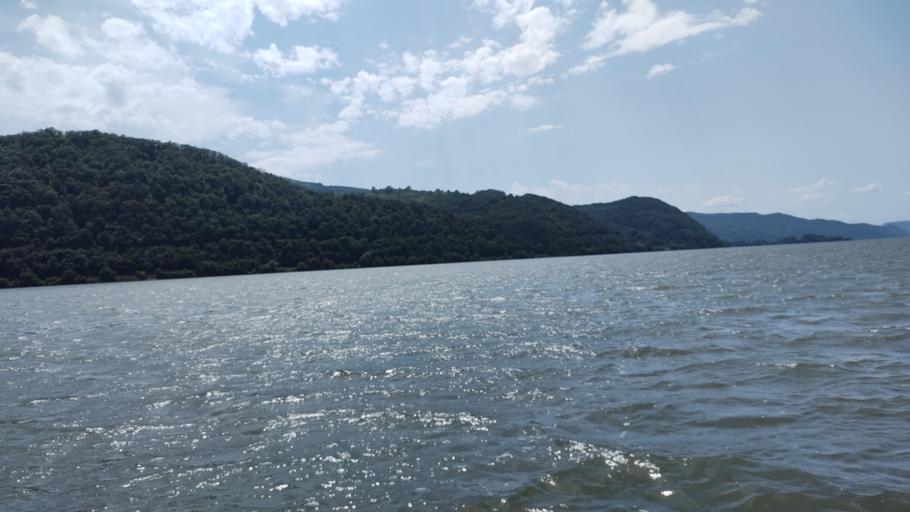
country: RO
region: Caras-Severin
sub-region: Comuna Berzasca
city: Liubcova
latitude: 44.6497
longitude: 21.8792
